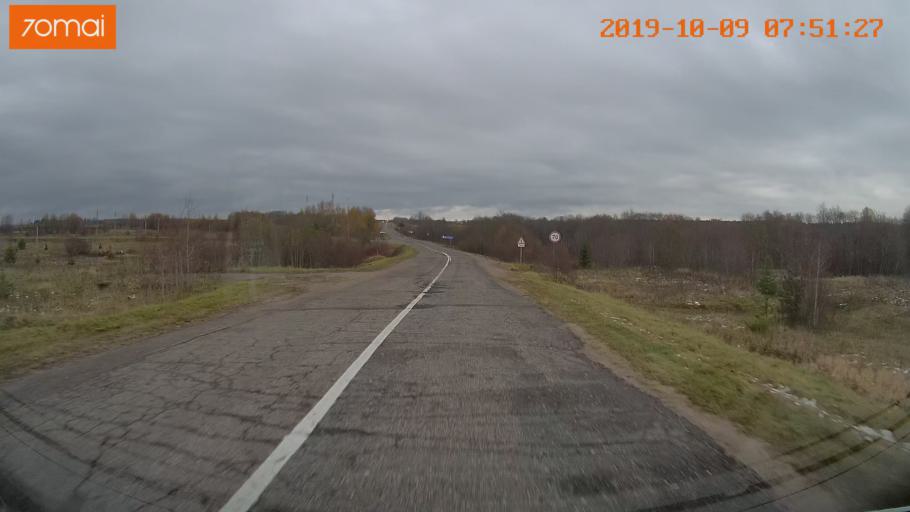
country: RU
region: Jaroslavl
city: Kukoboy
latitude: 58.6830
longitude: 39.8782
